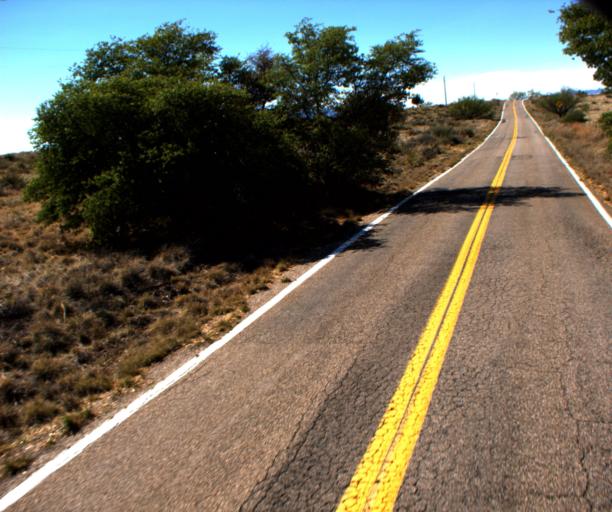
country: US
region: Arizona
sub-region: Cochise County
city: Huachuca City
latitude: 31.5839
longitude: -110.5609
